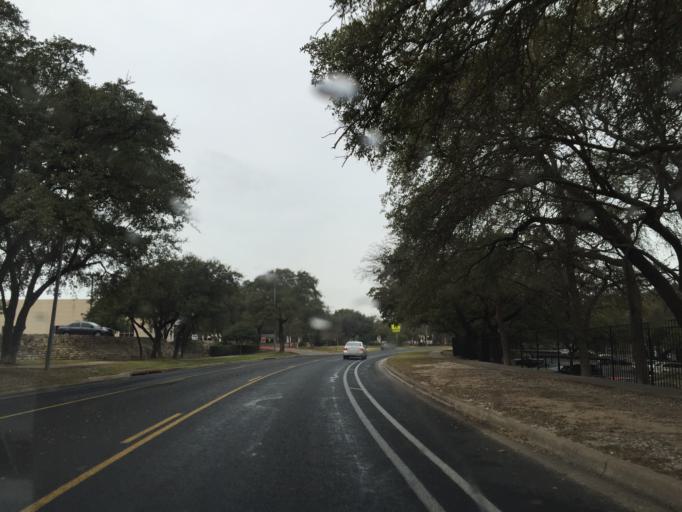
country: US
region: Texas
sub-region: Travis County
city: Wells Branch
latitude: 30.3994
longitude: -97.7065
